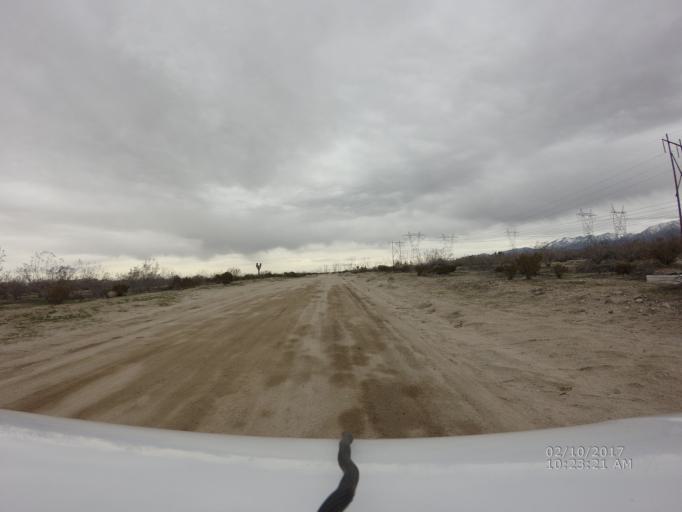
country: US
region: California
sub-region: Los Angeles County
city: Littlerock
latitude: 34.5139
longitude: -117.9578
